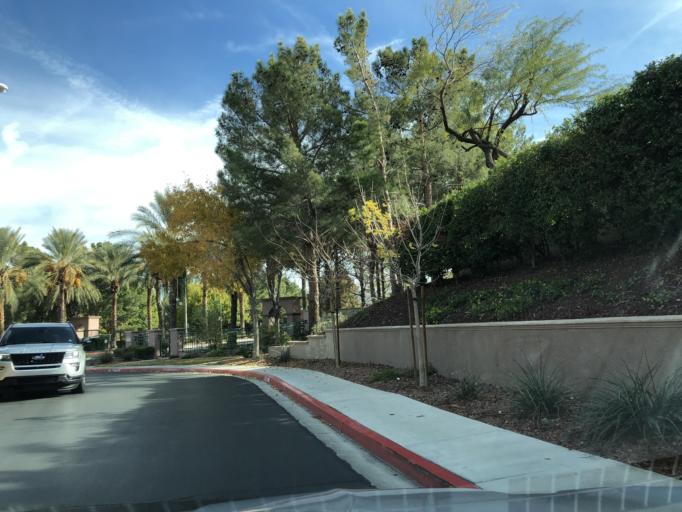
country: US
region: Nevada
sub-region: Clark County
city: Whitney
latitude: 36.0143
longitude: -115.0879
